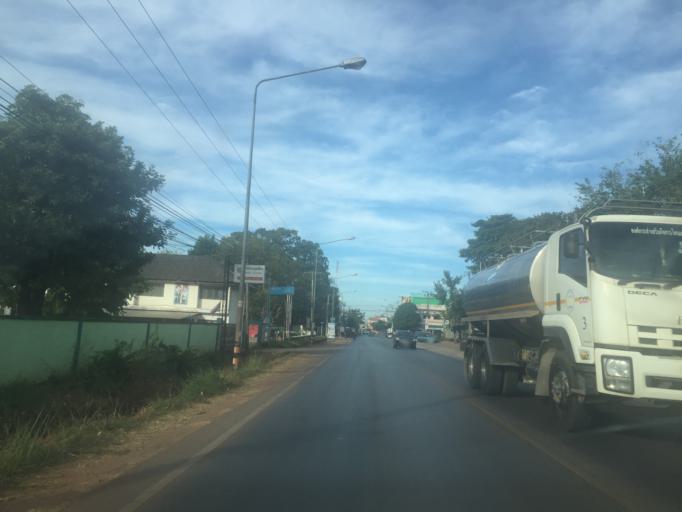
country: TH
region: Changwat Udon Thani
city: Si That
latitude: 16.9745
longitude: 103.2174
